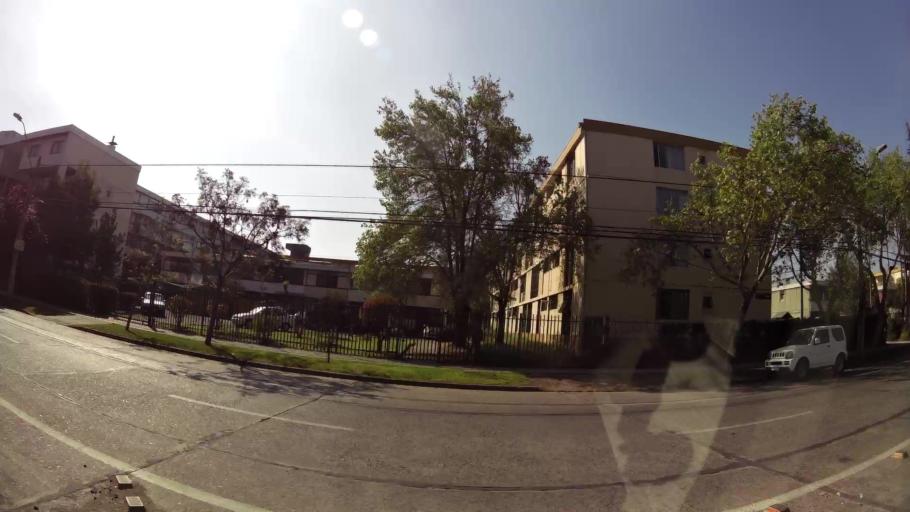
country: CL
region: Santiago Metropolitan
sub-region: Provincia de Santiago
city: Santiago
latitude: -33.4664
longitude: -70.6206
